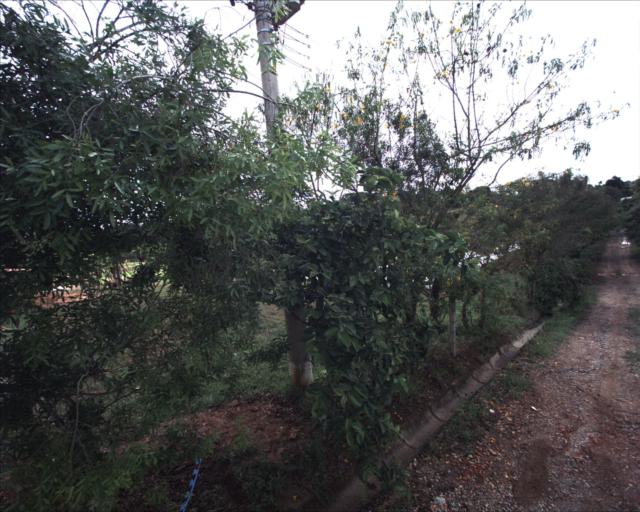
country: BR
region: Sao Paulo
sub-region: Aracoiaba Da Serra
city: Aracoiaba da Serra
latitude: -23.5512
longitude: -47.5501
